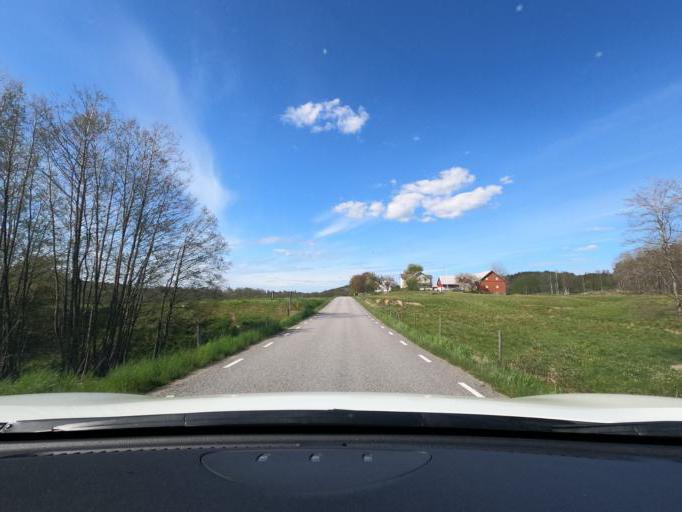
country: SE
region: Vaestra Goetaland
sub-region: Harryda Kommun
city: Ravlanda
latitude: 57.6211
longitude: 12.4972
